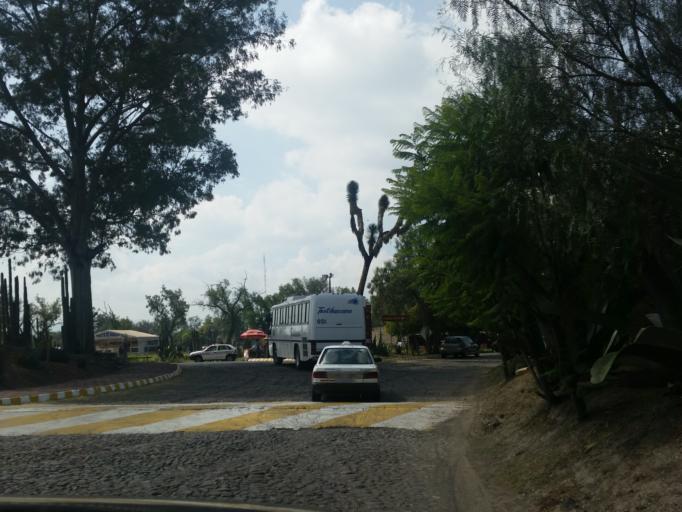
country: MX
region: Mexico
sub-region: Teotihuacan
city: Teotihuacan de Arista
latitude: 19.6838
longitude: -98.8533
